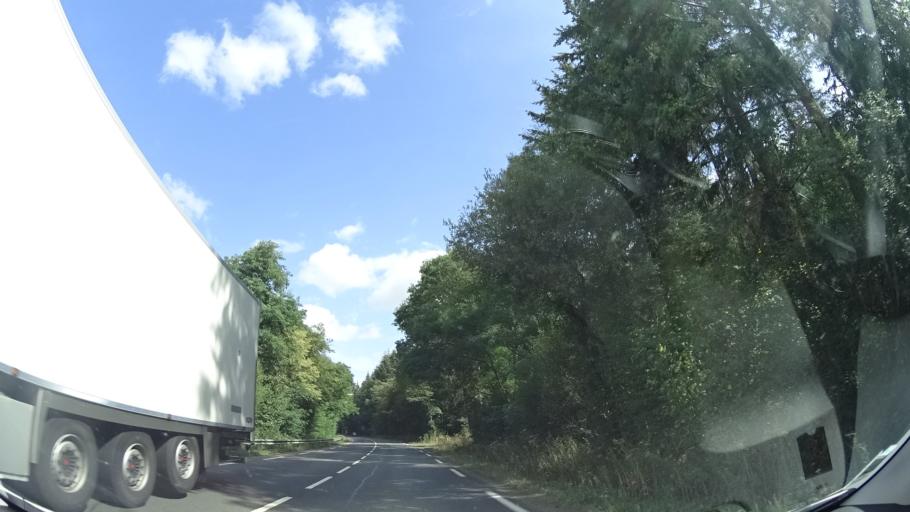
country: FR
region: Pays de la Loire
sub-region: Departement de la Sarthe
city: Brulon
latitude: 48.0267
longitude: -0.2553
